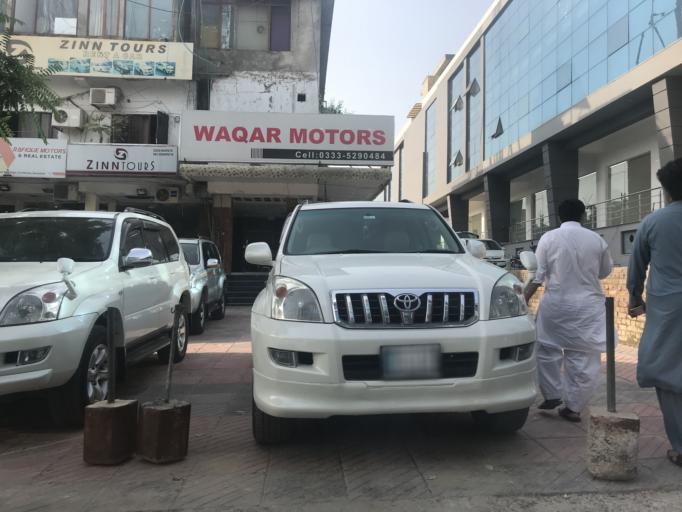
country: PK
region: Islamabad
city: Islamabad
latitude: 33.6981
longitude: 73.0486
